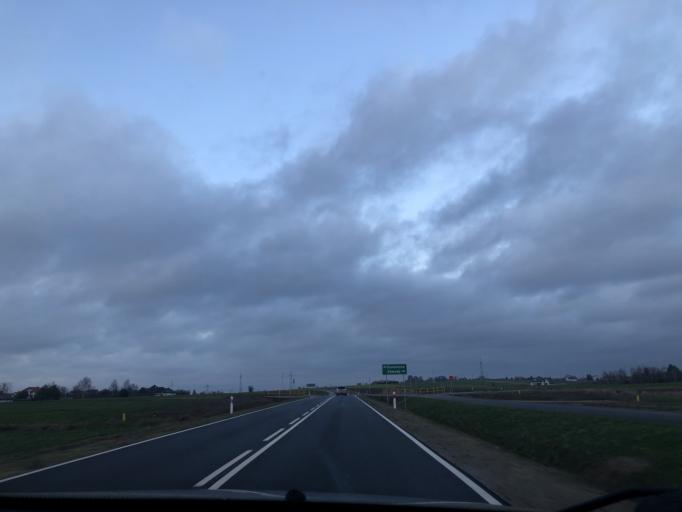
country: PL
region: Podlasie
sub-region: Lomza
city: Lomza
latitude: 53.1421
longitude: 22.0520
